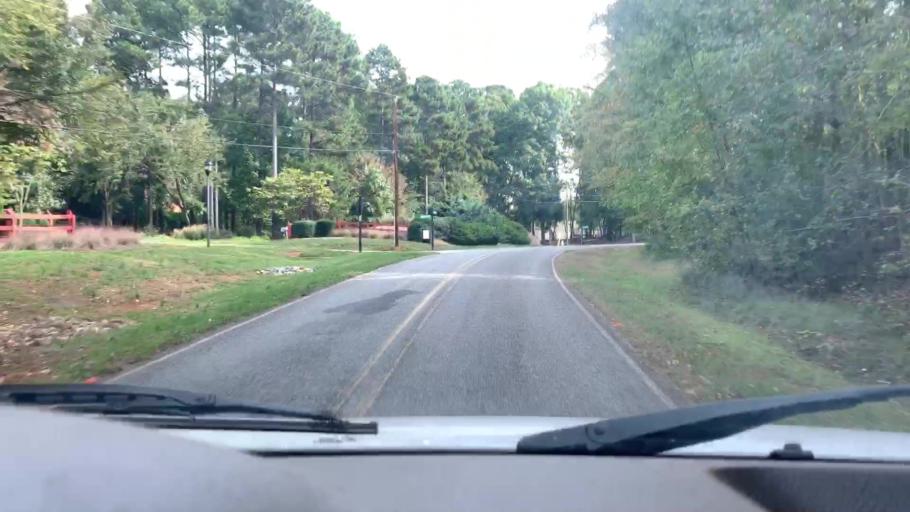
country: US
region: North Carolina
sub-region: Catawba County
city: Lake Norman of Catawba
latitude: 35.5743
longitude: -80.9440
